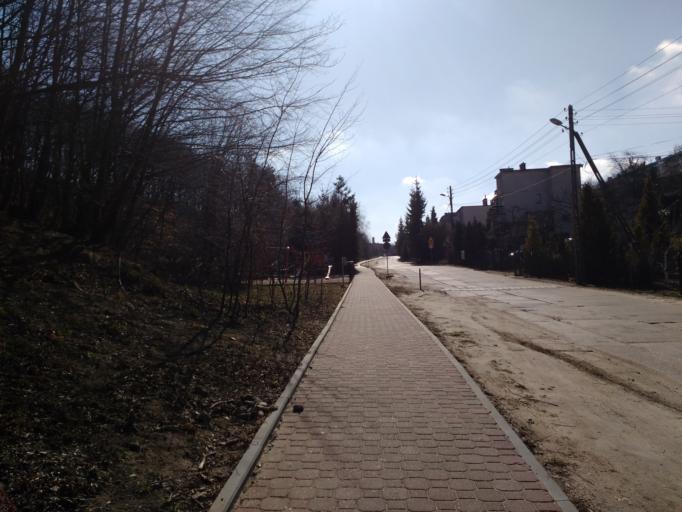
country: PL
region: Pomeranian Voivodeship
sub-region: Gdynia
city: Wielki Kack
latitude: 54.4760
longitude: 18.5117
